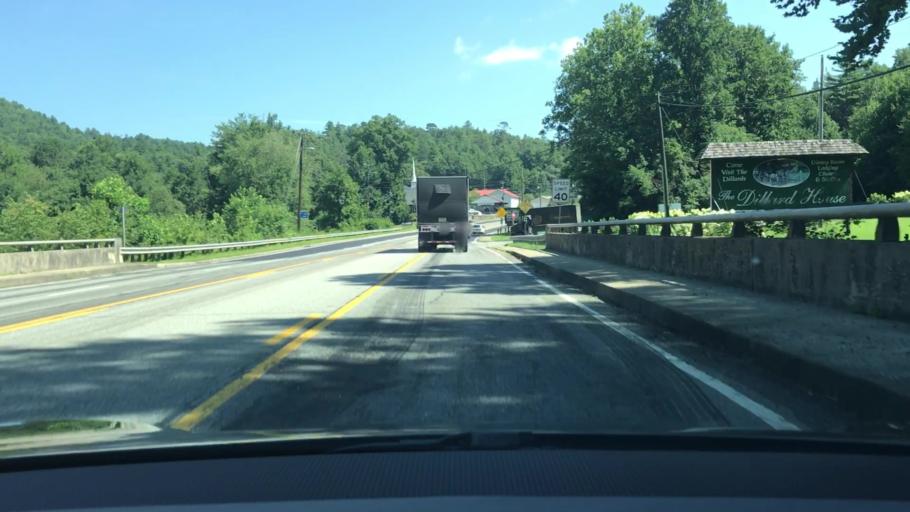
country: US
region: Georgia
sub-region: Rabun County
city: Mountain City
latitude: 34.9675
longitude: -83.3884
